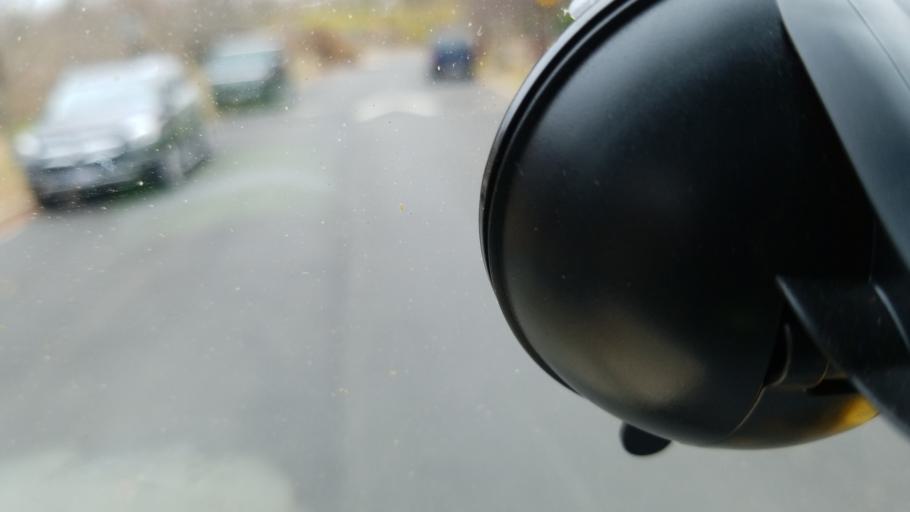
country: US
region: Maryland
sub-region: Prince George's County
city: Silver Hill
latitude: 38.8777
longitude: -76.9655
